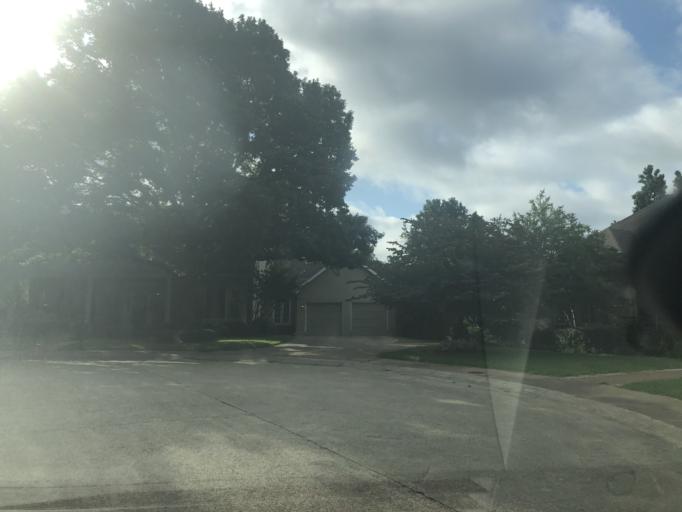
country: US
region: Texas
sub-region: Dallas County
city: University Park
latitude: 32.8667
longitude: -96.8362
